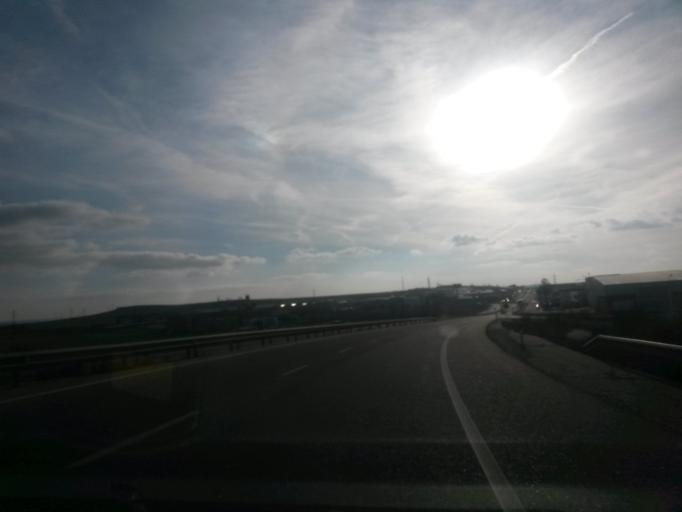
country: ES
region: Castille and Leon
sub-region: Provincia de Salamanca
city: Villares de la Reina
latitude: 40.9993
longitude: -5.6290
